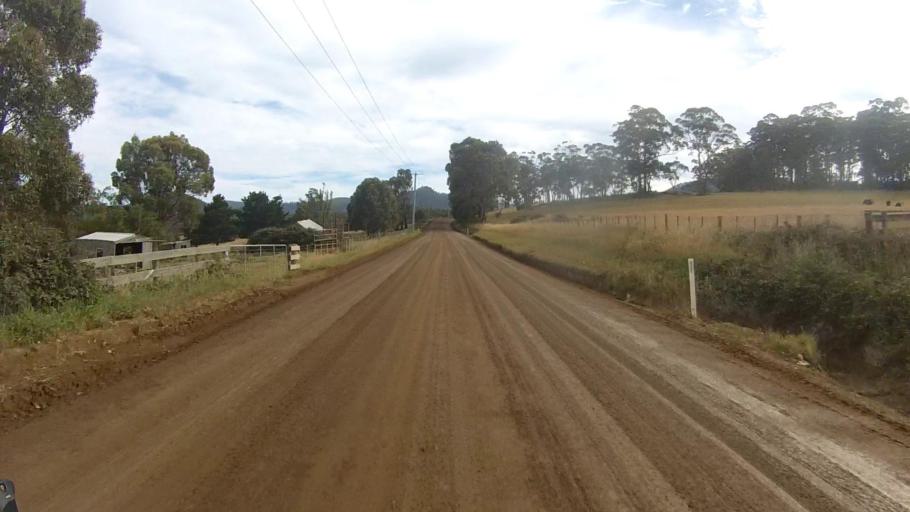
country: AU
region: Tasmania
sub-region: Sorell
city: Sorell
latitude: -42.7856
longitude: 147.8077
